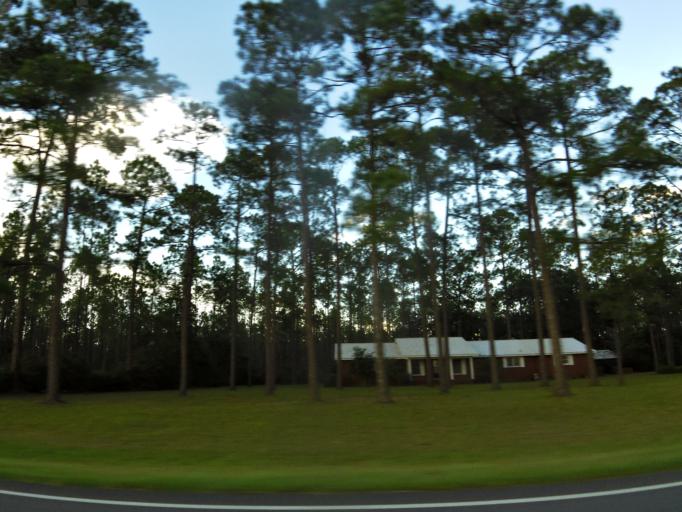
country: US
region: Georgia
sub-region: Echols County
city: Statenville
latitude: 30.7639
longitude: -83.1271
